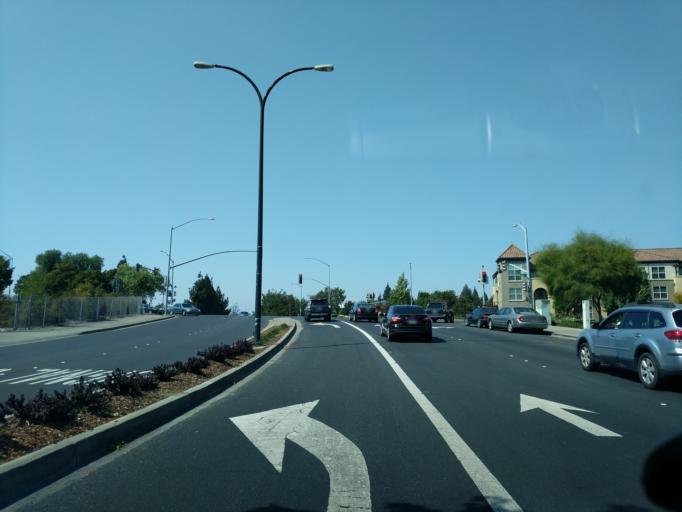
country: US
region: California
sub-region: Contra Costa County
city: Waldon
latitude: 37.9327
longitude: -122.0588
